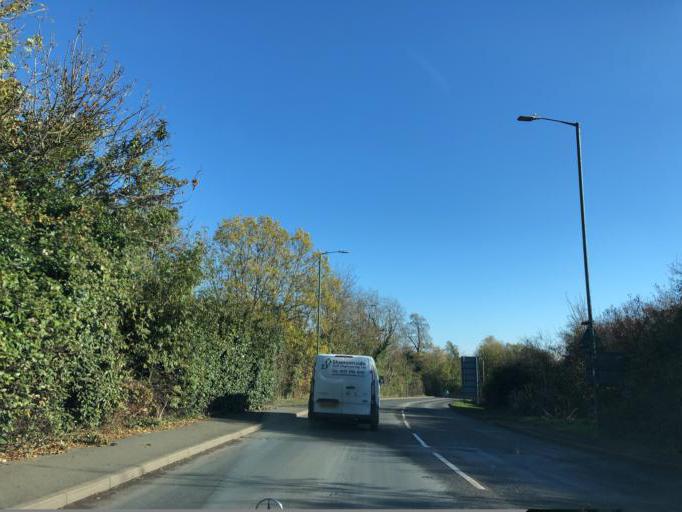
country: GB
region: England
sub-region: Warwickshire
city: Southam
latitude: 52.2486
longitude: -1.3971
